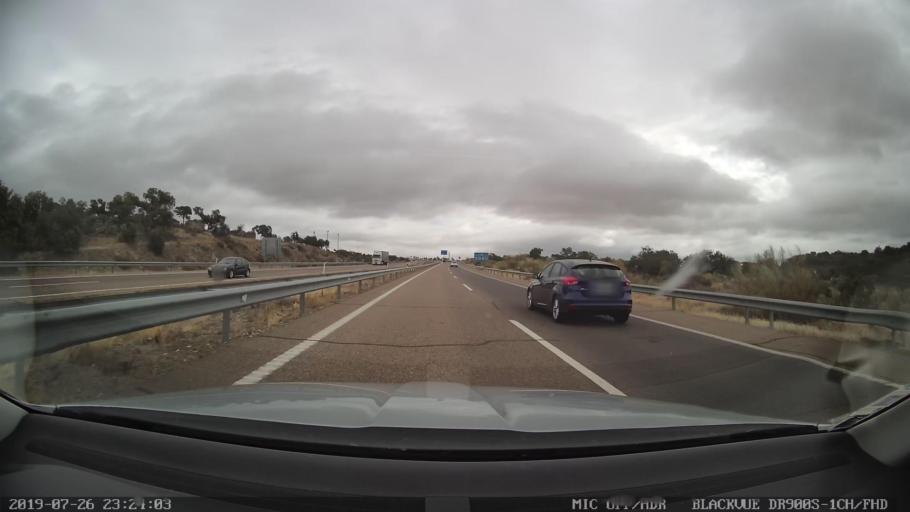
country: ES
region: Extremadura
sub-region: Provincia de Caceres
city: Miajadas
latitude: 39.1680
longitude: -5.9092
